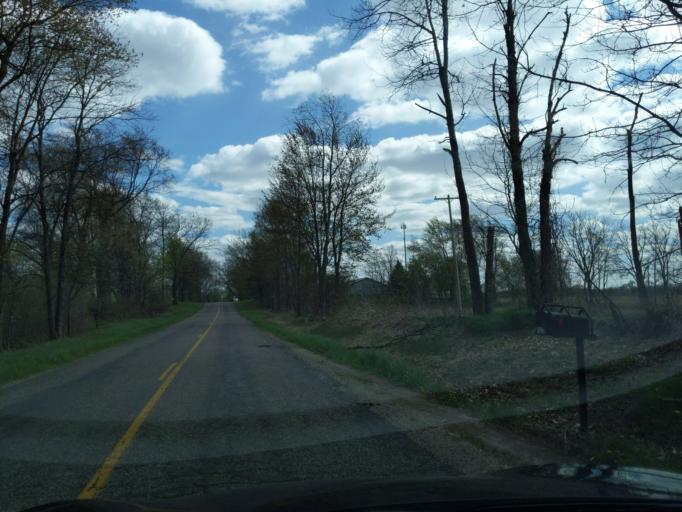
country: US
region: Michigan
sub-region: Ingham County
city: Leslie
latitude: 42.4772
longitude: -84.5412
